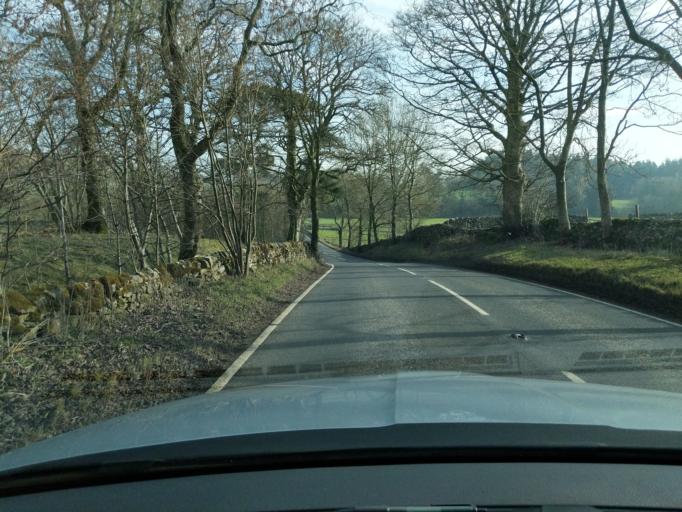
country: GB
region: England
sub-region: North Yorkshire
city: Leyburn
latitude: 54.3556
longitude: -1.8168
